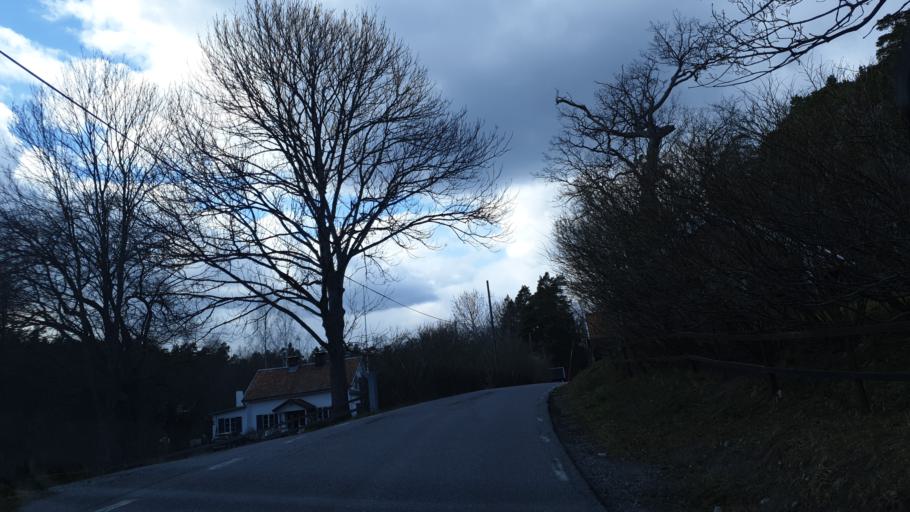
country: SE
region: Stockholm
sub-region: Tyreso Kommun
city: Brevik
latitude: 59.2425
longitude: 18.4460
